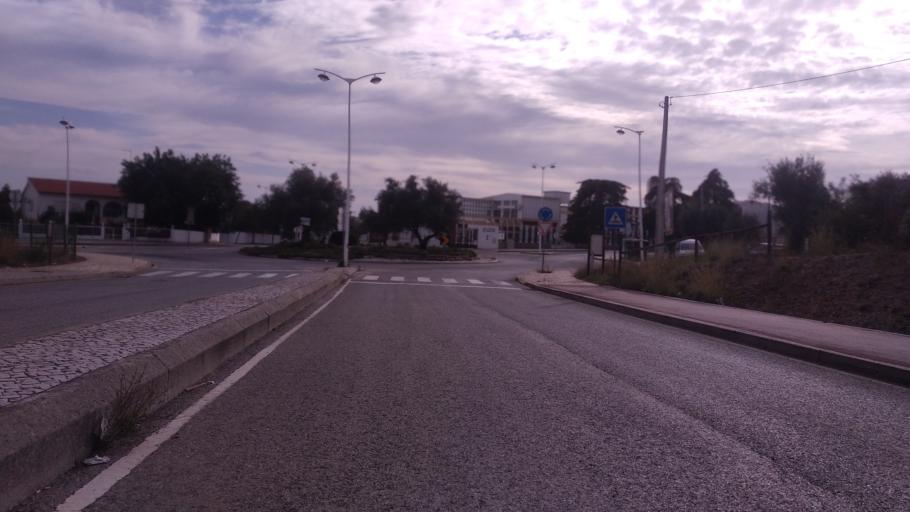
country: PT
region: Faro
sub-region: Sao Bras de Alportel
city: Sao Bras de Alportel
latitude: 37.1539
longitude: -7.8978
